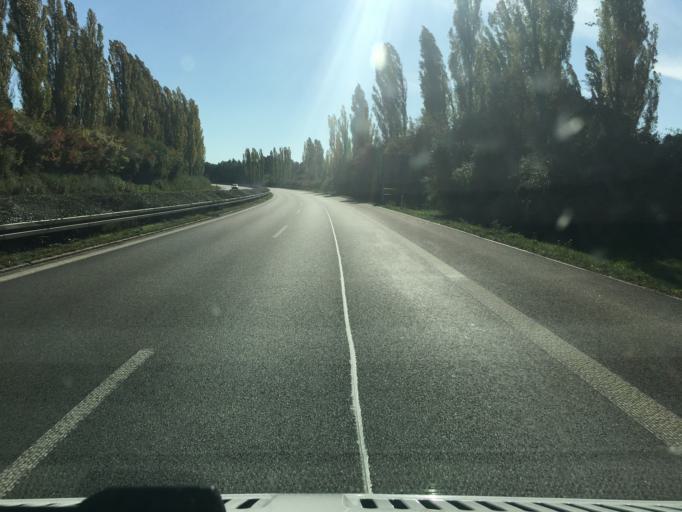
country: DE
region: Saxony
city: Weissenborn
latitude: 50.7752
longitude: 12.4937
